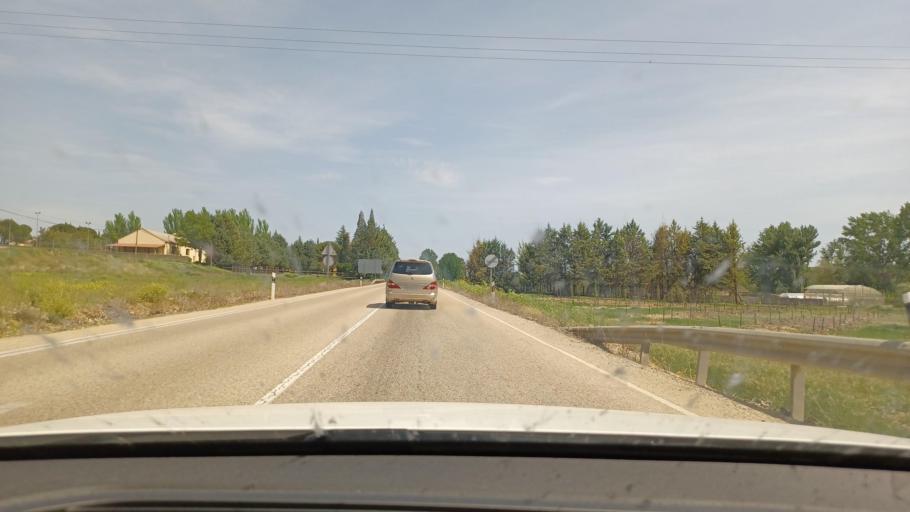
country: ES
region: Castille and Leon
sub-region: Provincia de Soria
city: Almazan
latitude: 41.4761
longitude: -2.5501
